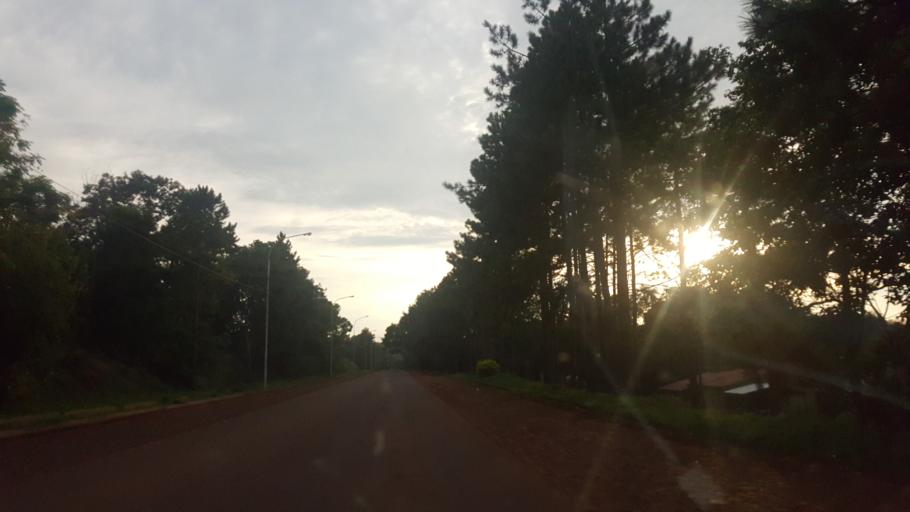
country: AR
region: Misiones
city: Dos de Mayo
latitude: -27.0366
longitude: -54.6843
